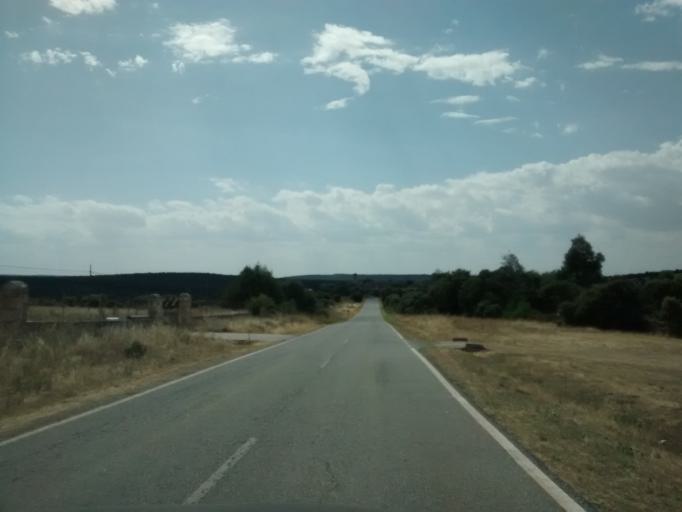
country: ES
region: Castille and Leon
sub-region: Provincia de Segovia
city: Pedraza
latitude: 41.1296
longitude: -3.7979
